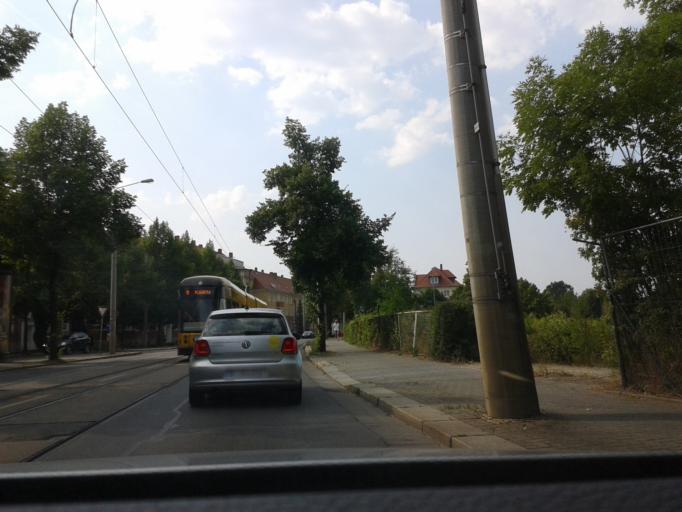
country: DE
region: Saxony
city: Dresden
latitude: 51.0137
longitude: 13.7902
